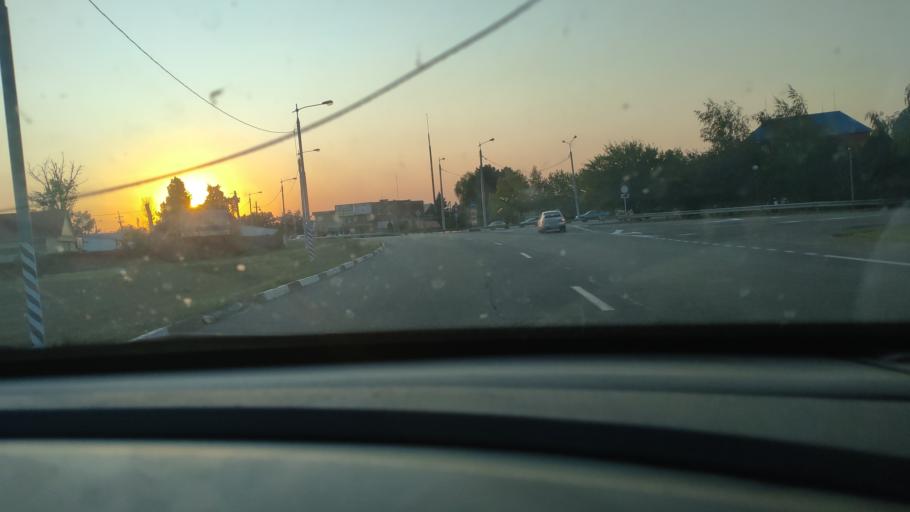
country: RU
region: Krasnodarskiy
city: Timashevsk
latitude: 45.6002
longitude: 38.9322
